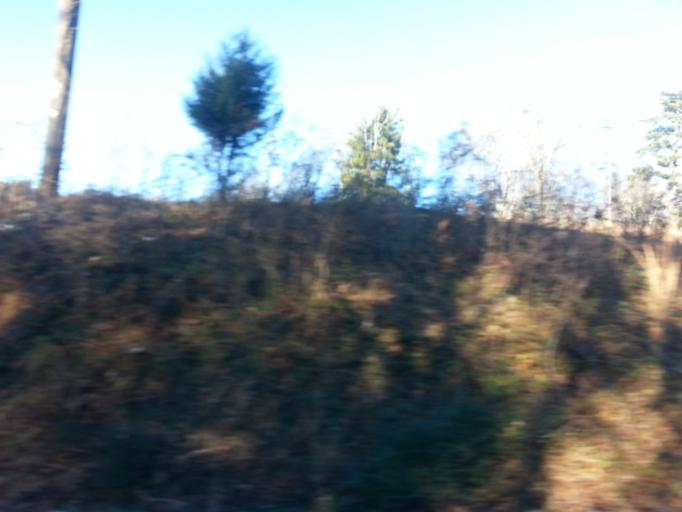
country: US
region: Tennessee
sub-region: Blount County
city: Louisville
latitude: 35.8893
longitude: -83.9860
